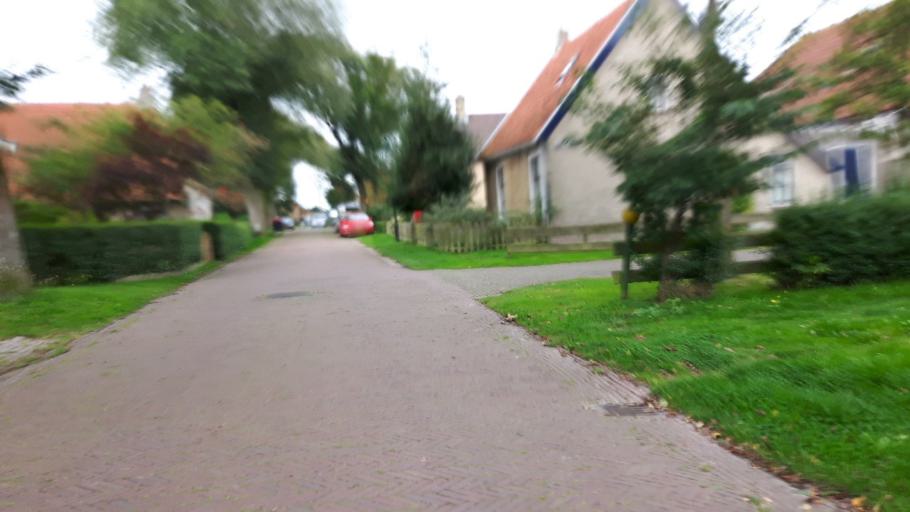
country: NL
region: Friesland
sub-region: Gemeente Ameland
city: Hollum
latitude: 53.4438
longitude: 5.6893
